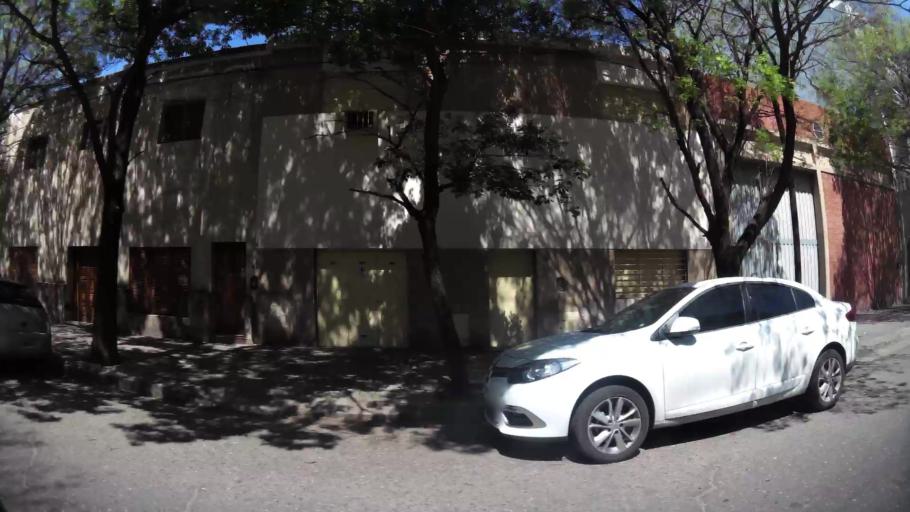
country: AR
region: Cordoba
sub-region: Departamento de Capital
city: Cordoba
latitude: -31.3976
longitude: -64.1851
